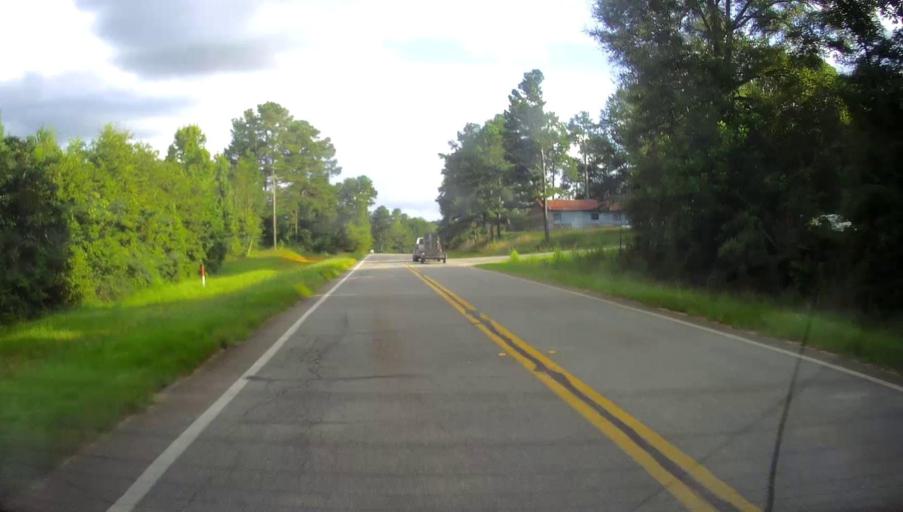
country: US
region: Georgia
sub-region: Crawford County
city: Roberta
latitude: 32.8035
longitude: -84.0302
